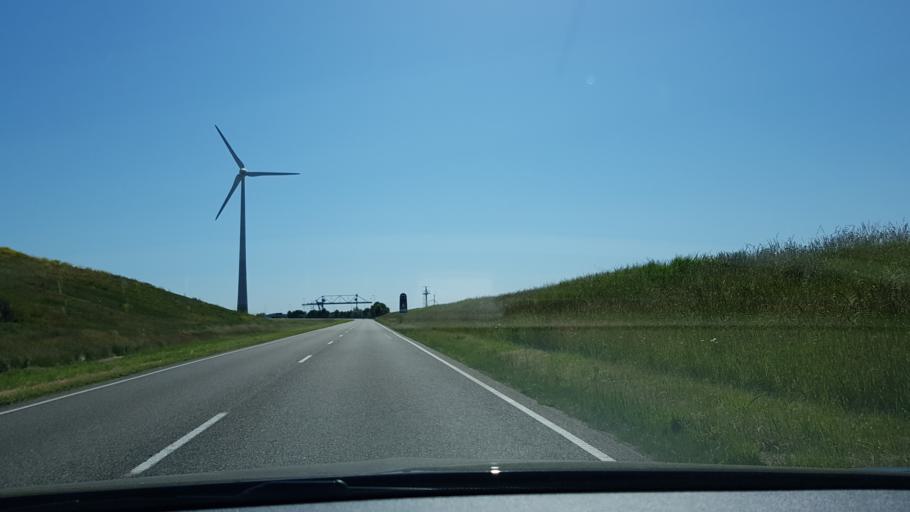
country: NL
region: North Holland
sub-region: Gemeente Zaanstad
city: Zaanstad
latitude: 52.4328
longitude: 4.7425
